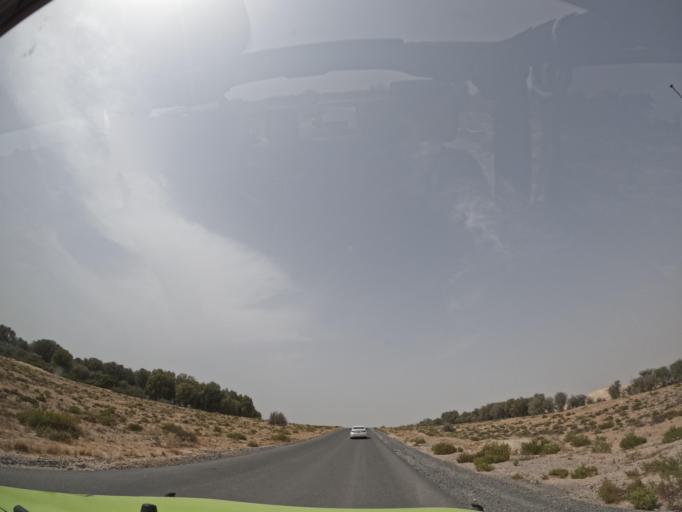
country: AE
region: Dubai
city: Dubai
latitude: 25.1426
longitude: 55.3407
